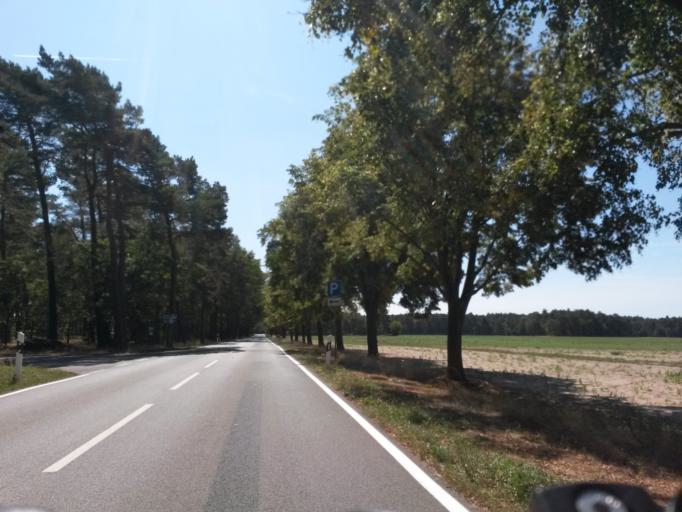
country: DE
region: Saxony-Anhalt
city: Hassel
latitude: 52.6404
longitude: 11.9492
